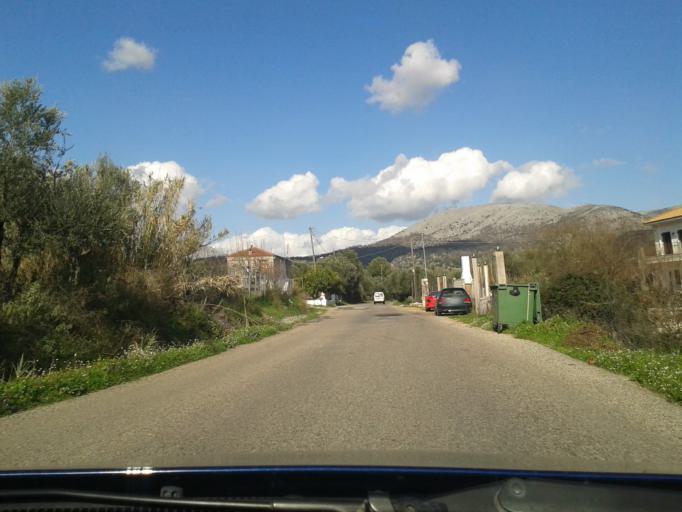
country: GR
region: West Greece
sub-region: Nomos Aitolias kai Akarnanias
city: Astakos
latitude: 38.5554
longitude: 21.0964
